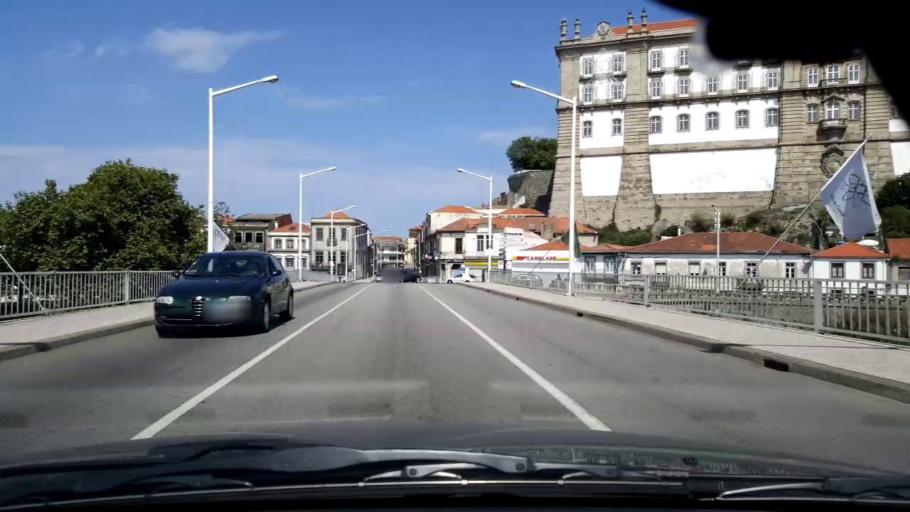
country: PT
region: Porto
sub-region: Vila do Conde
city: Vila do Conde
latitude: 41.3512
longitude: -8.7394
